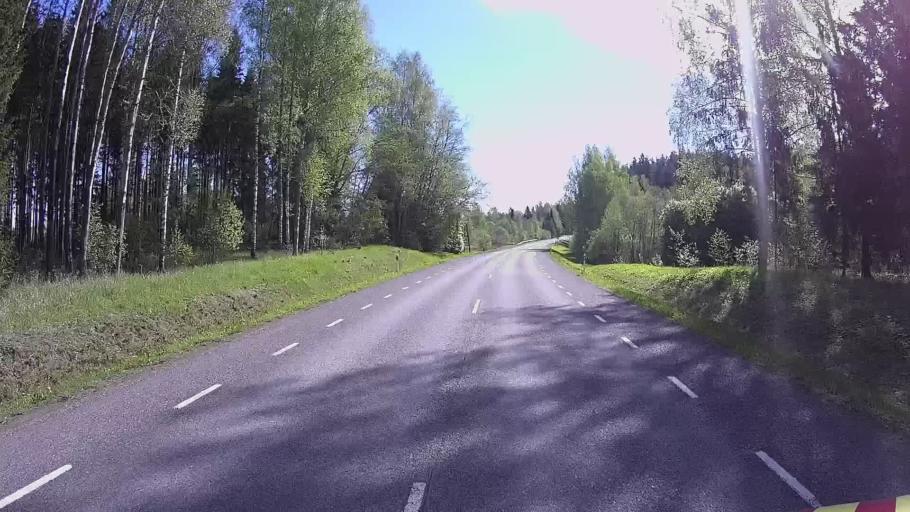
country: EE
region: Polvamaa
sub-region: Raepina vald
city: Rapina
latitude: 58.1023
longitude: 27.3681
